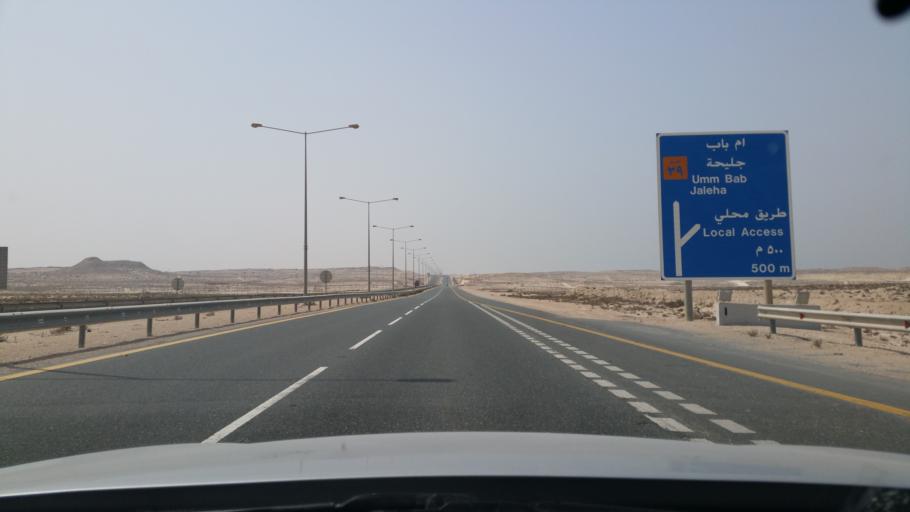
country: QA
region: Baladiyat ar Rayyan
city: Dukhan
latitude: 25.3706
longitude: 50.7803
